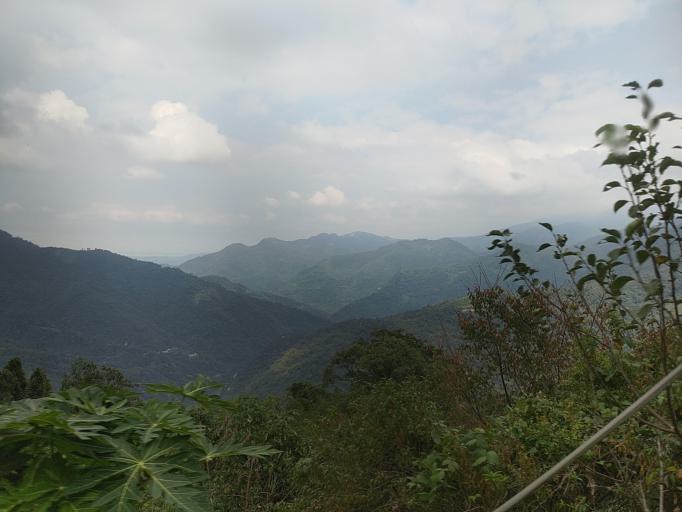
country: TW
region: Taiwan
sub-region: Hsinchu
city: Hsinchu
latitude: 24.6117
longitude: 121.0979
